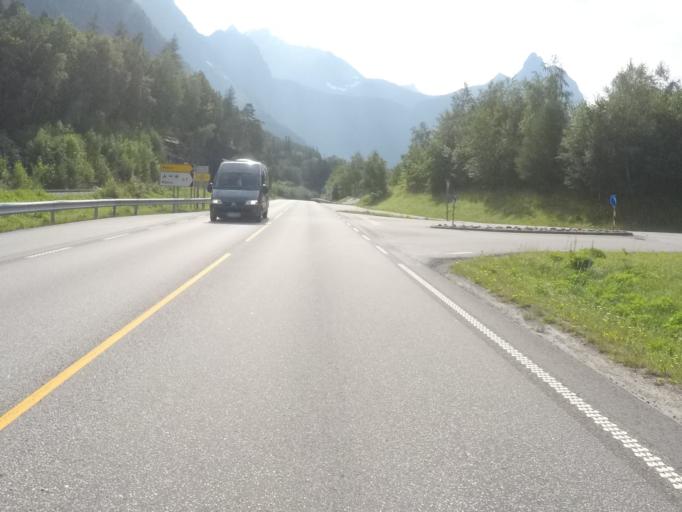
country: NO
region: More og Romsdal
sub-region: Rauma
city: Andalsnes
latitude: 62.5398
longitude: 7.7243
